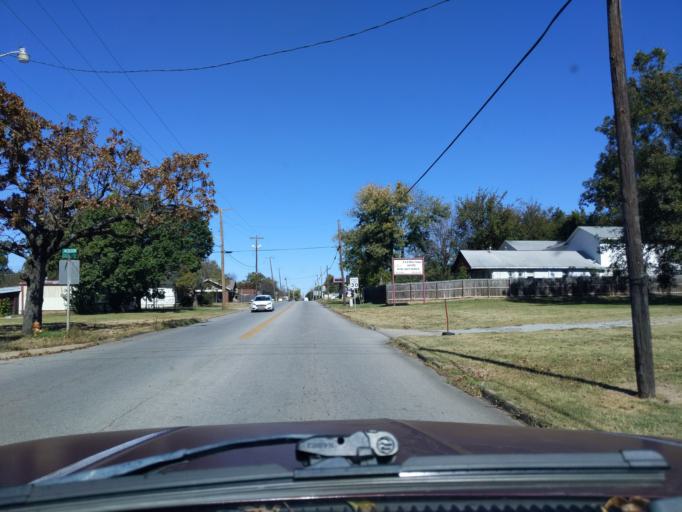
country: US
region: Oklahoma
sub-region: Creek County
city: Bristow
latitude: 35.8257
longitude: -96.3872
